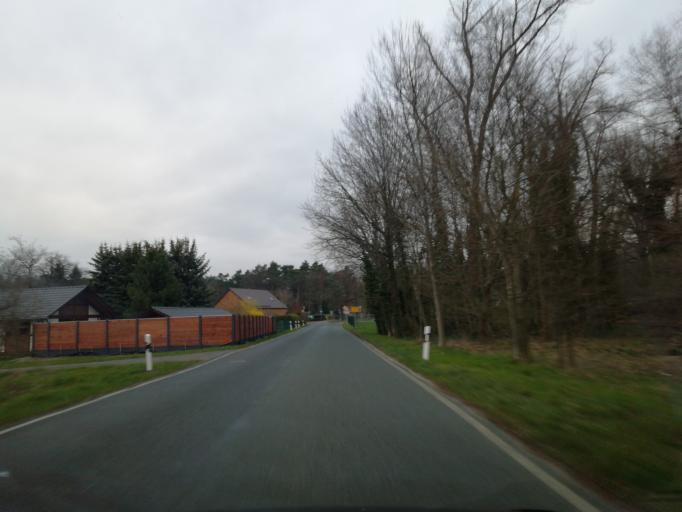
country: DE
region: Brandenburg
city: Vetschau
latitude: 51.7668
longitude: 14.0822
